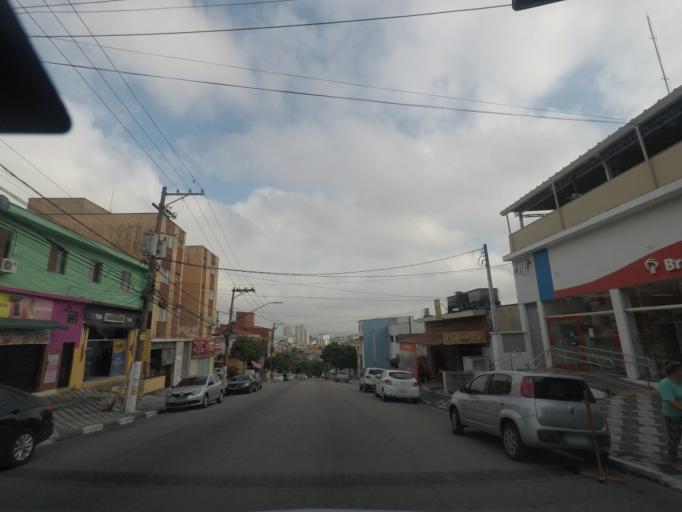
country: BR
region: Sao Paulo
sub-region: Osasco
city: Osasco
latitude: -23.5703
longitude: -46.7786
